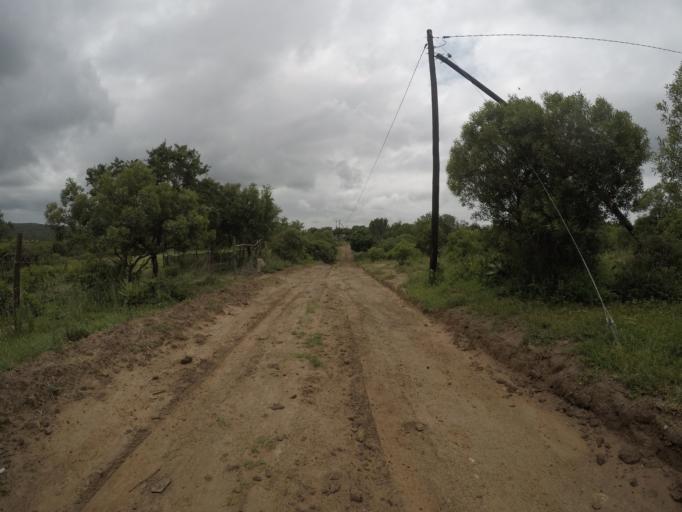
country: ZA
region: KwaZulu-Natal
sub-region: uThungulu District Municipality
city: Empangeni
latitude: -28.6039
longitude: 31.8278
